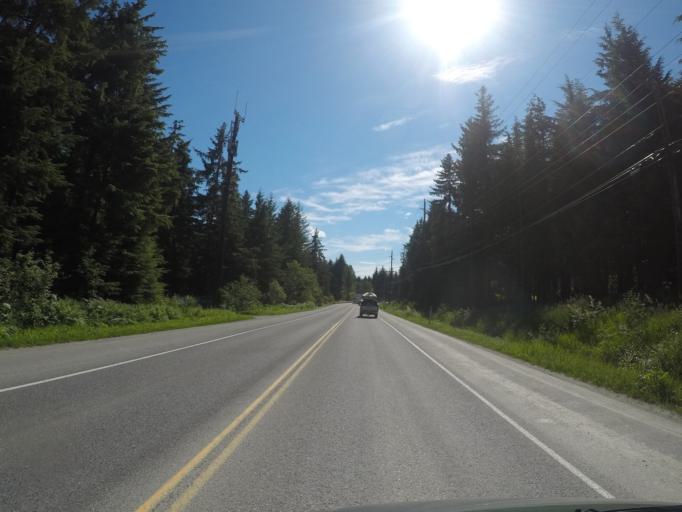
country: US
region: Alaska
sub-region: Juneau City and Borough
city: Juneau
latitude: 58.3846
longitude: -134.6600
